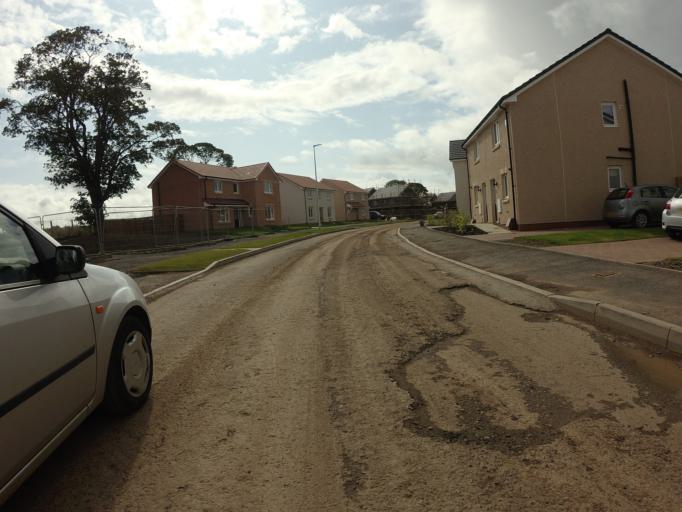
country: GB
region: Scotland
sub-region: East Lothian
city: Musselburgh
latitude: 55.9386
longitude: -3.0280
